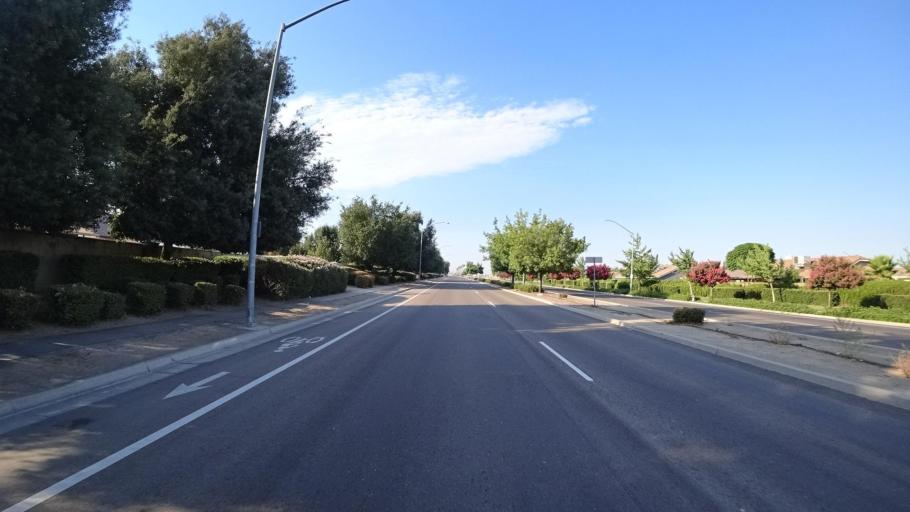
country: US
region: California
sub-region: Fresno County
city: Sunnyside
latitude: 36.7137
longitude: -119.6999
